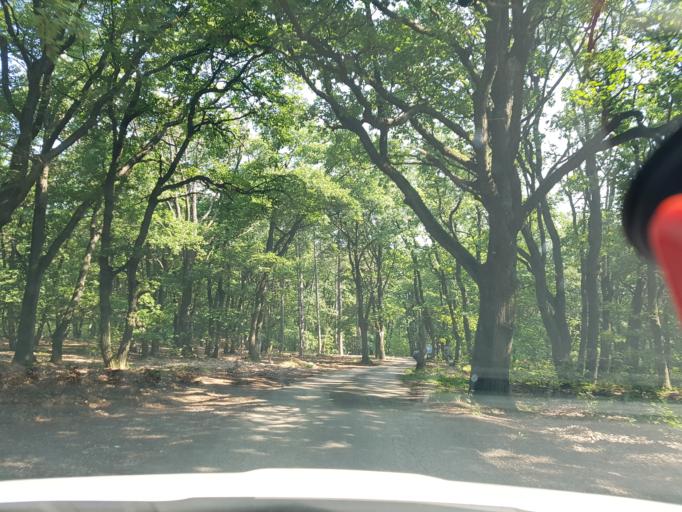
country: HU
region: Veszprem
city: Balatonalmadi
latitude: 47.0077
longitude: 17.9901
